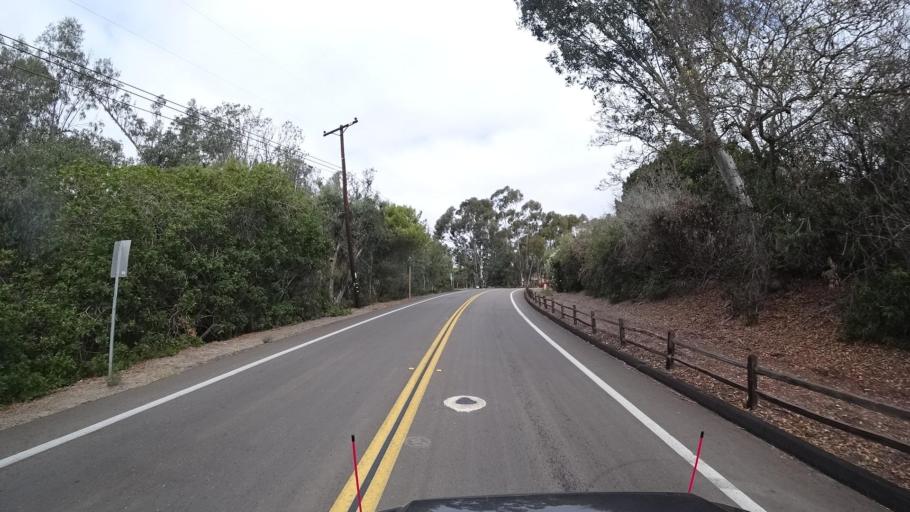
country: US
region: California
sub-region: San Diego County
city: Rancho Santa Fe
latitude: 33.0237
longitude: -117.2302
